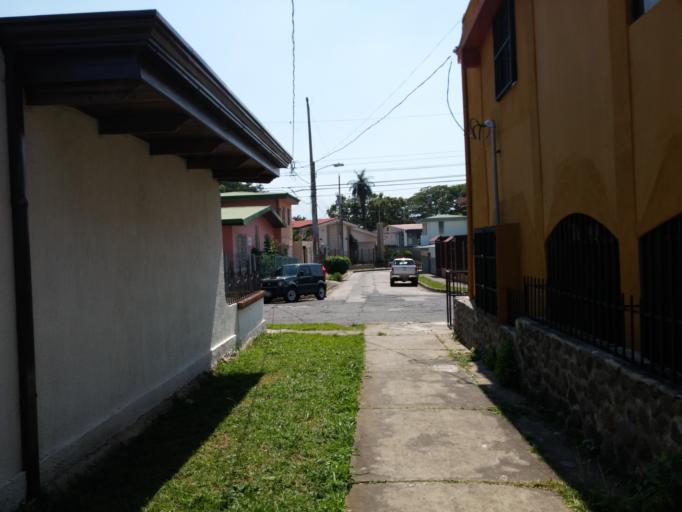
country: CR
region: Alajuela
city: Alajuela
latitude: 10.0125
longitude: -84.2087
